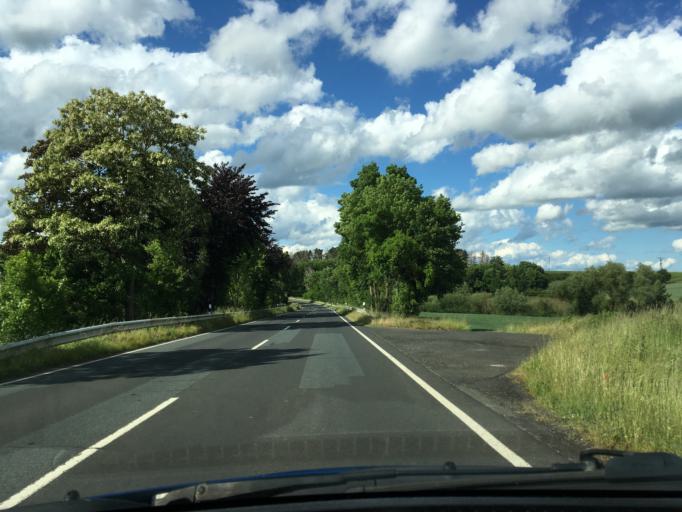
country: DE
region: Lower Saxony
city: Moringen
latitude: 51.7094
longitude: 9.8748
